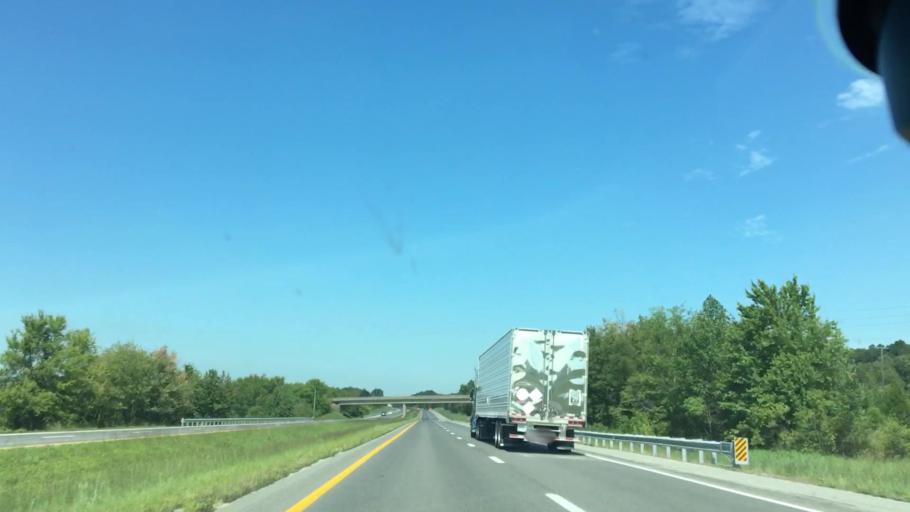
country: US
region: Kentucky
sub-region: Webster County
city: Sebree
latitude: 37.5076
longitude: -87.4747
